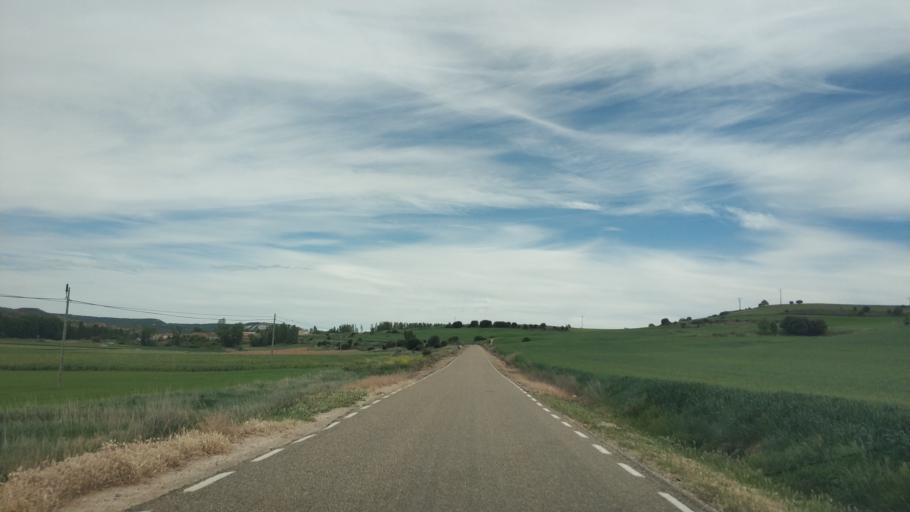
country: ES
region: Castille and Leon
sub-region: Provincia de Soria
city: Berlanga de Duero
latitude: 41.4447
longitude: -2.8308
